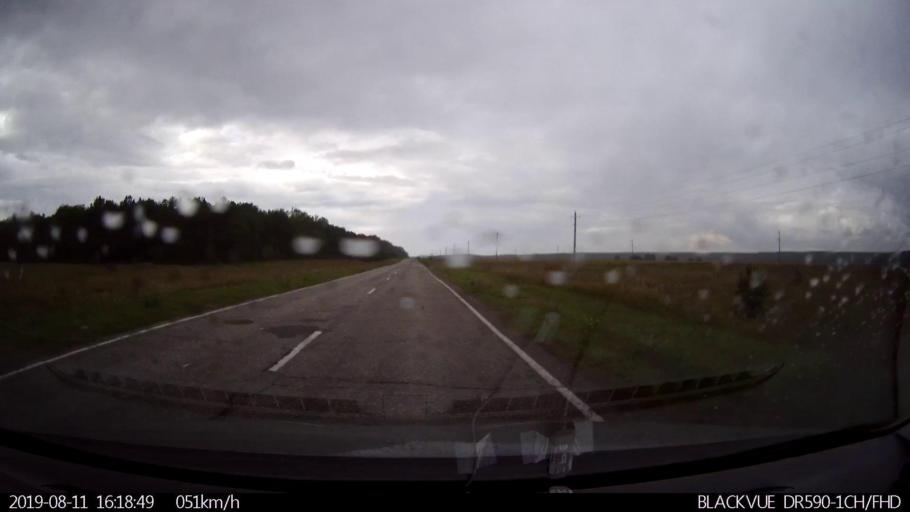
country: RU
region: Ulyanovsk
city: Mayna
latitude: 54.0580
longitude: 47.6106
